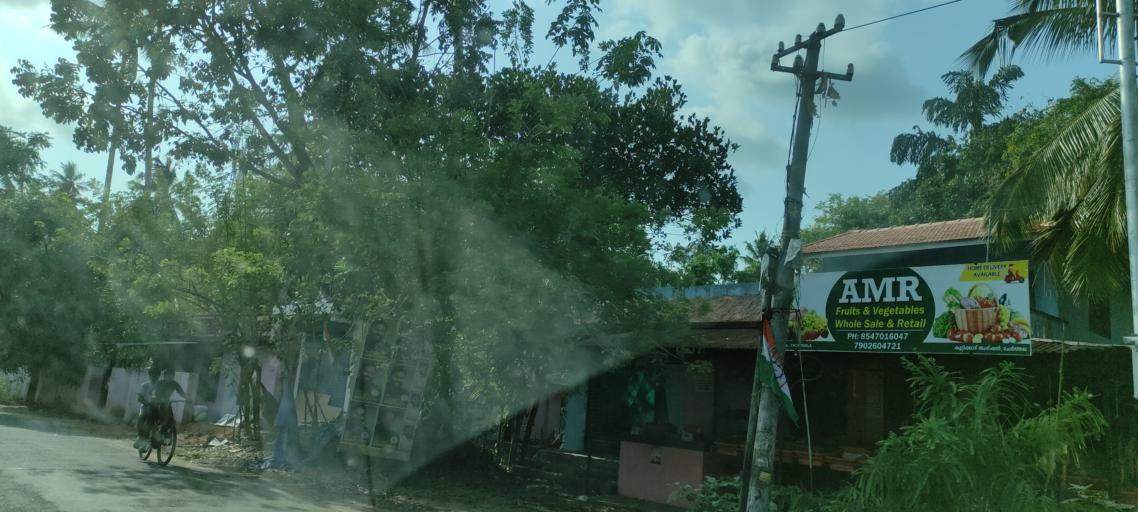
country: IN
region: Kerala
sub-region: Alappuzha
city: Vayalar
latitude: 9.6876
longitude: 76.3250
